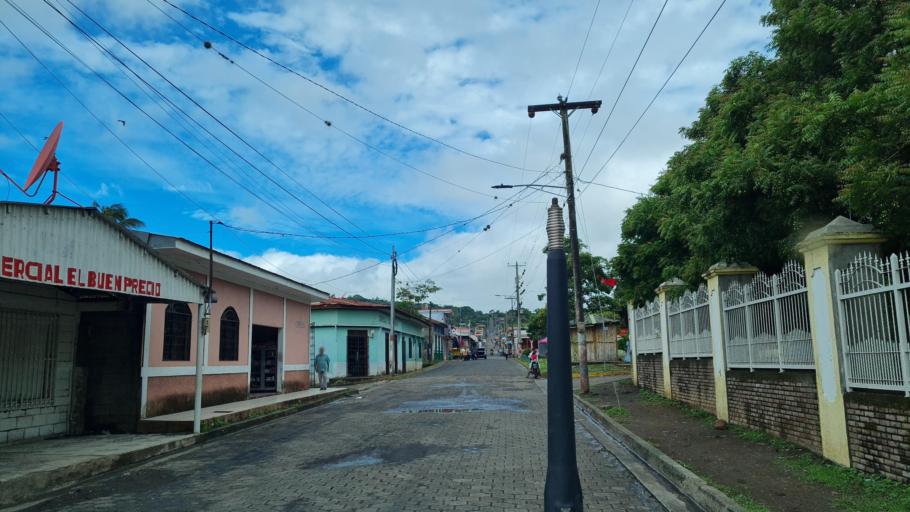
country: NI
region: Boaco
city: San Jose de los Remates
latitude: 12.6665
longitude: -85.7852
